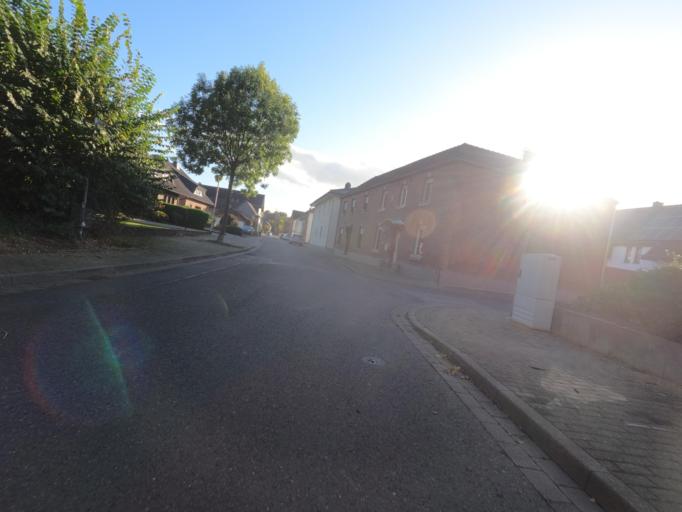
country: DE
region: North Rhine-Westphalia
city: Huckelhoven
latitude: 51.0186
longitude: 6.1775
